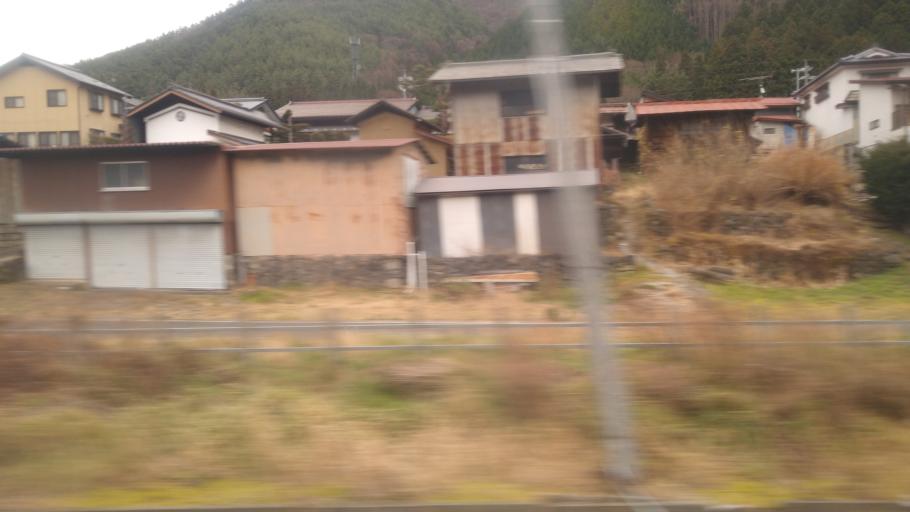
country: JP
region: Nagano
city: Shiojiri
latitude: 36.0610
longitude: 137.9006
